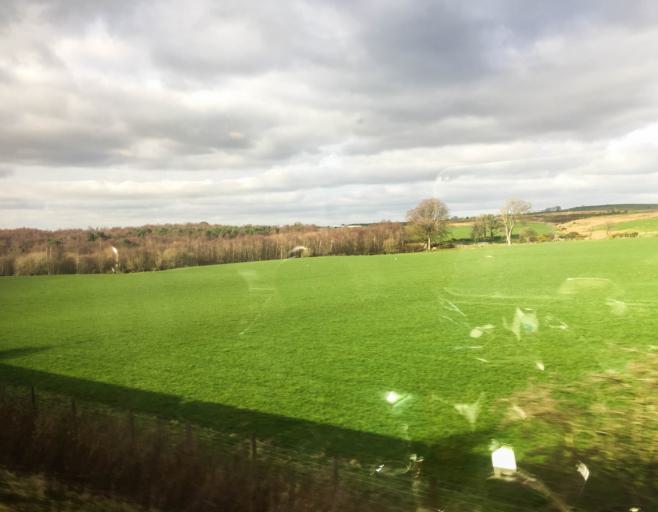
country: GB
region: Scotland
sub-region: South Lanarkshire
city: Carluke
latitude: 55.7047
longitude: -3.8182
